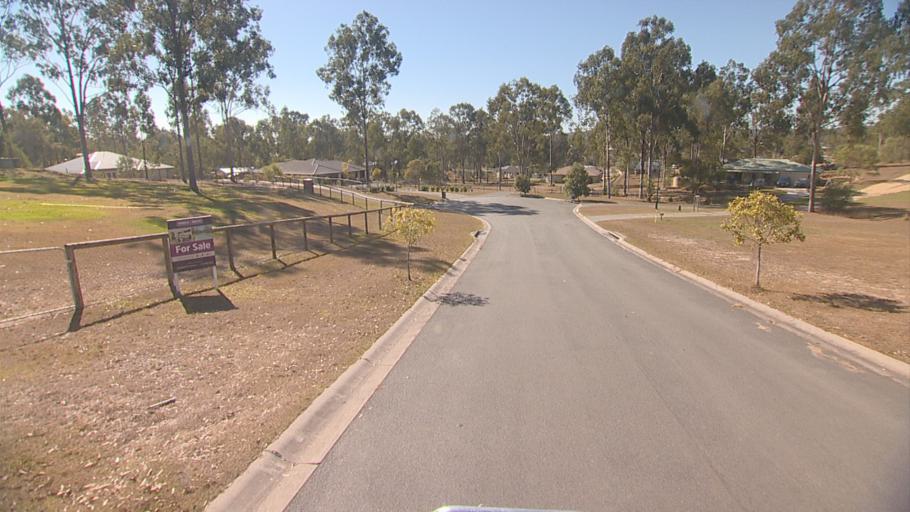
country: AU
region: Queensland
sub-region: Logan
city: Cedar Vale
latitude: -27.8711
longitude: 153.0382
